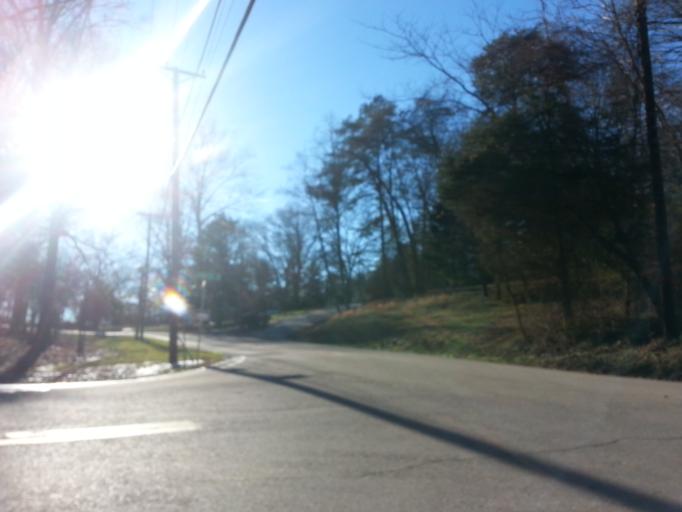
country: US
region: Tennessee
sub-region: Knox County
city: Knoxville
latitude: 35.9002
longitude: -83.9828
